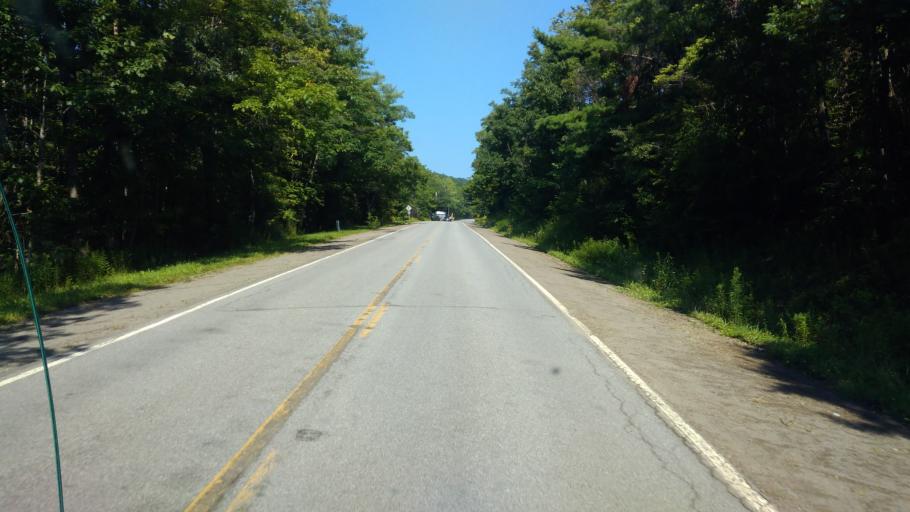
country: US
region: New York
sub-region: Allegany County
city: Bolivar
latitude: 42.0917
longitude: -78.1680
